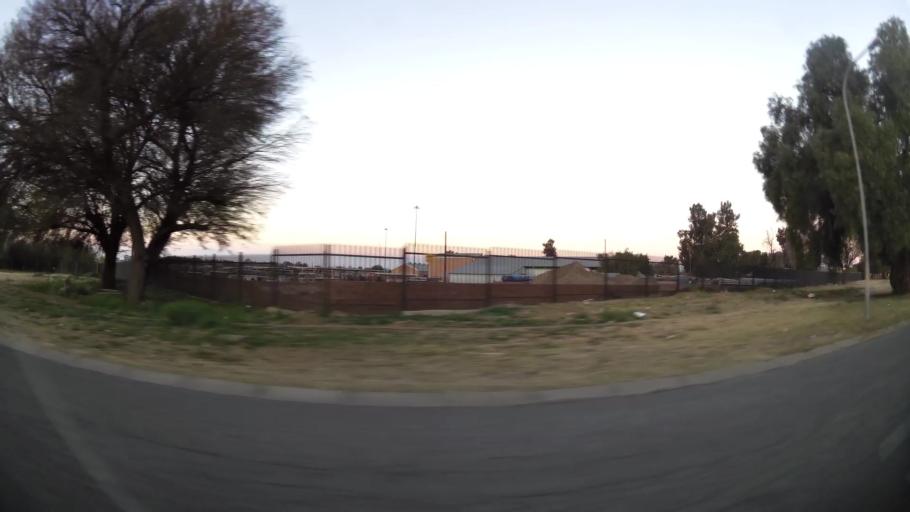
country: ZA
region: Northern Cape
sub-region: Frances Baard District Municipality
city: Kimberley
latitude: -28.7154
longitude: 24.7719
